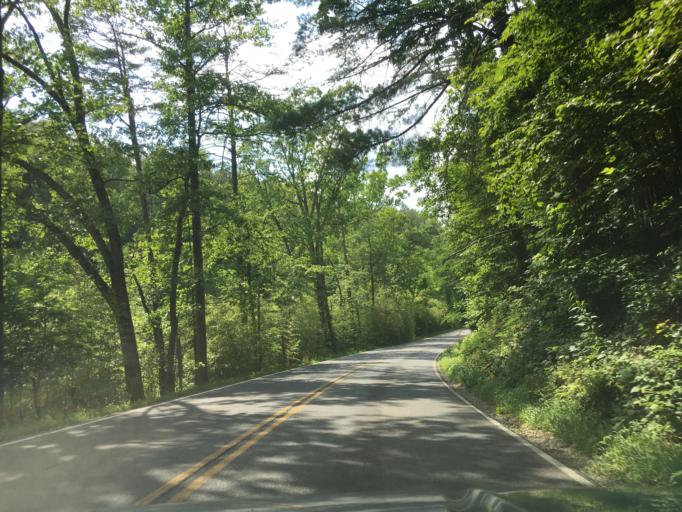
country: US
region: Virginia
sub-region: Roanoke County
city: Cave Spring
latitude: 37.2038
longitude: -80.0067
